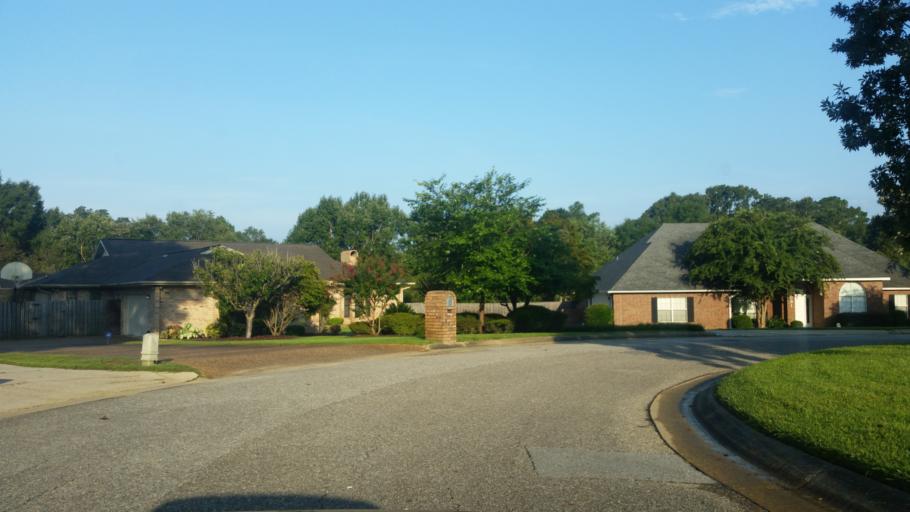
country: US
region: Florida
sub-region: Escambia County
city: Ferry Pass
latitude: 30.5371
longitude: -87.2279
